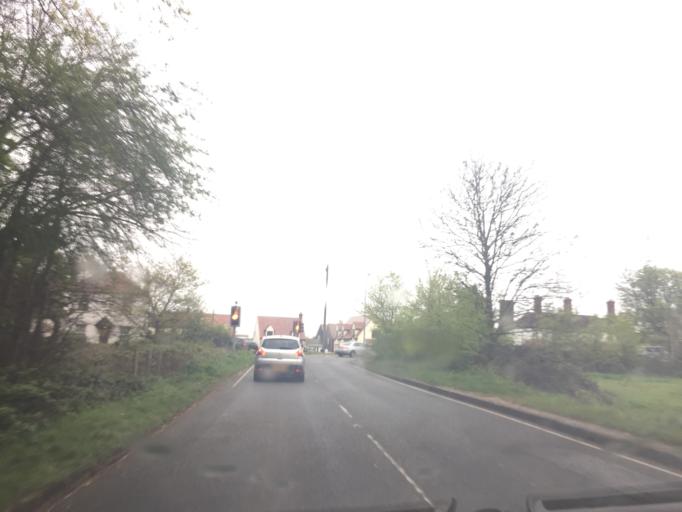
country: GB
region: England
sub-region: Essex
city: Epping
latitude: 51.6912
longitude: 0.0961
